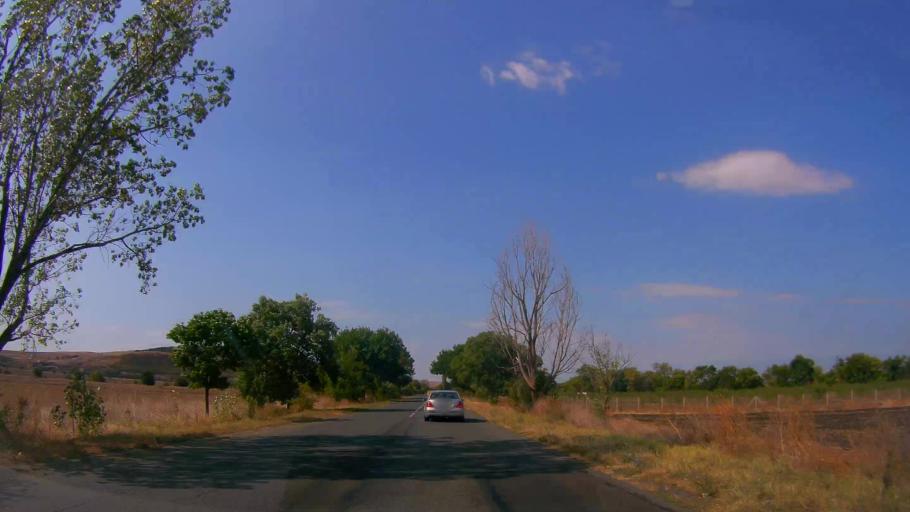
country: BG
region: Burgas
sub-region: Obshtina Karnobat
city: Karnobat
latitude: 42.6586
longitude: 27.0193
